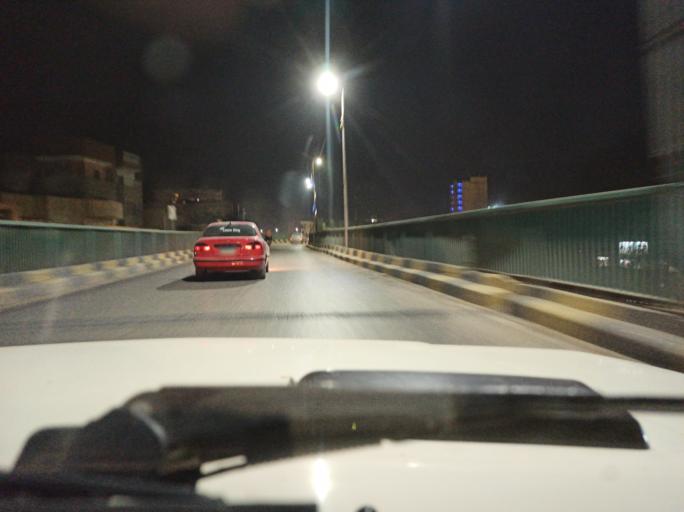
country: EG
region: Muhafazat Bani Suwayf
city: Bani Suwayf
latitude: 29.0763
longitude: 31.0924
